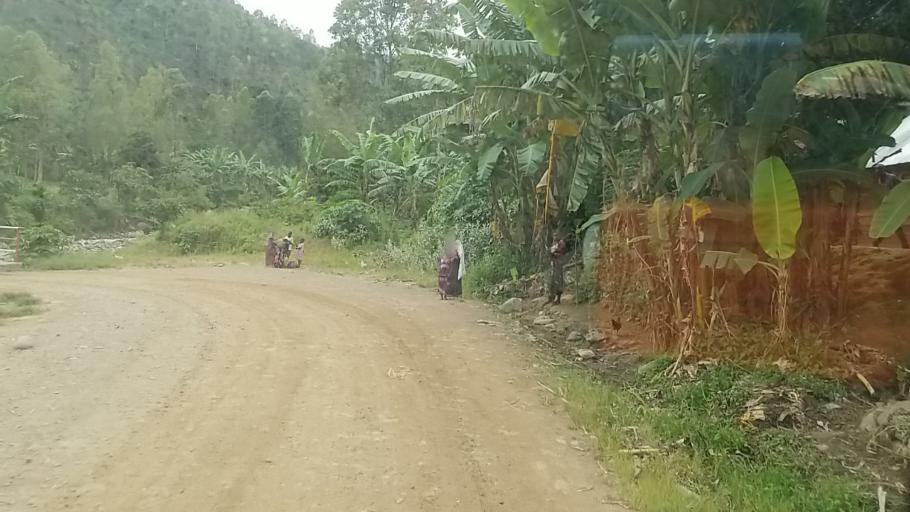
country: CD
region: Nord Kivu
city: Sake
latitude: -1.9523
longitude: 28.9254
